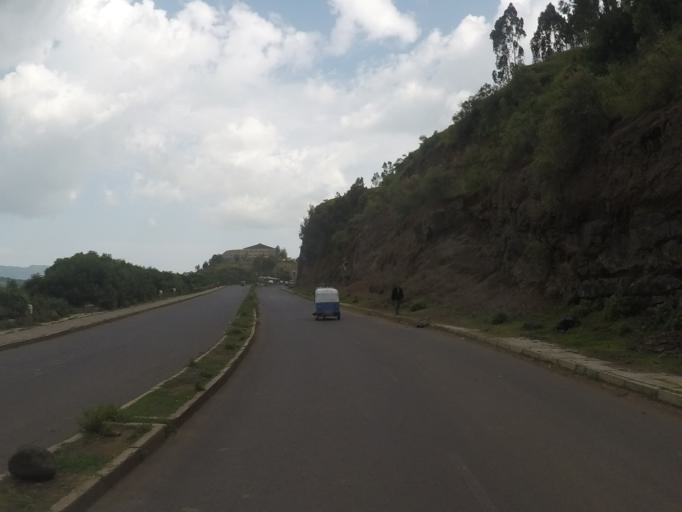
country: ET
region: Amhara
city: Gondar
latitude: 12.6305
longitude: 37.4688
